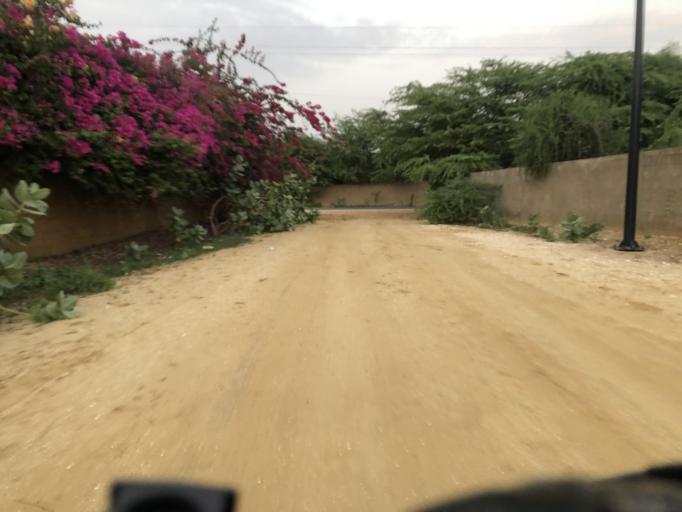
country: SN
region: Saint-Louis
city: Saint-Louis
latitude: 16.0644
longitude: -16.4296
